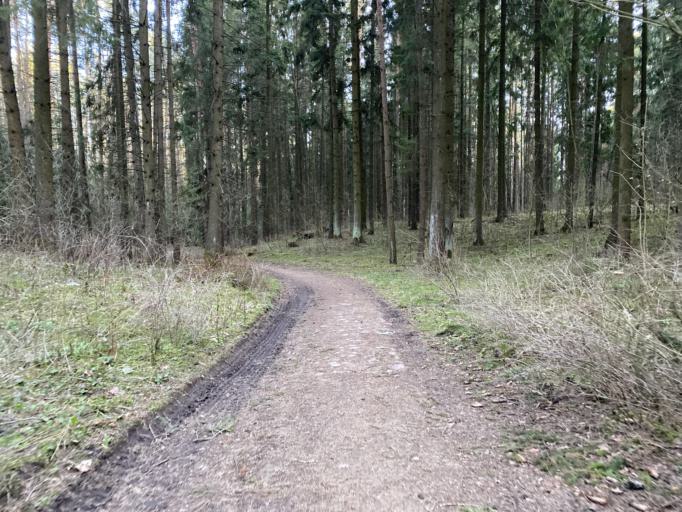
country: BY
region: Minsk
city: Borovlyany
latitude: 53.9485
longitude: 27.6560
